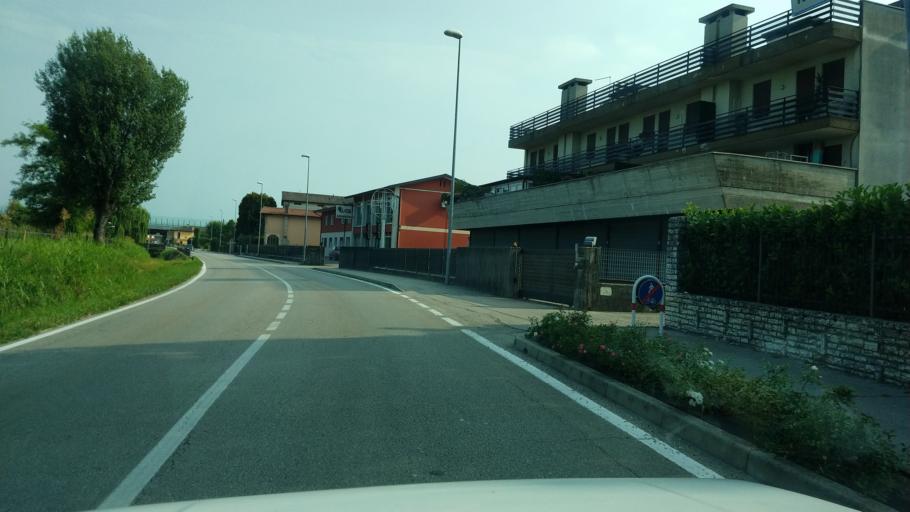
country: IT
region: Veneto
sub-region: Provincia di Vicenza
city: Nove
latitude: 45.7415
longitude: 11.6888
